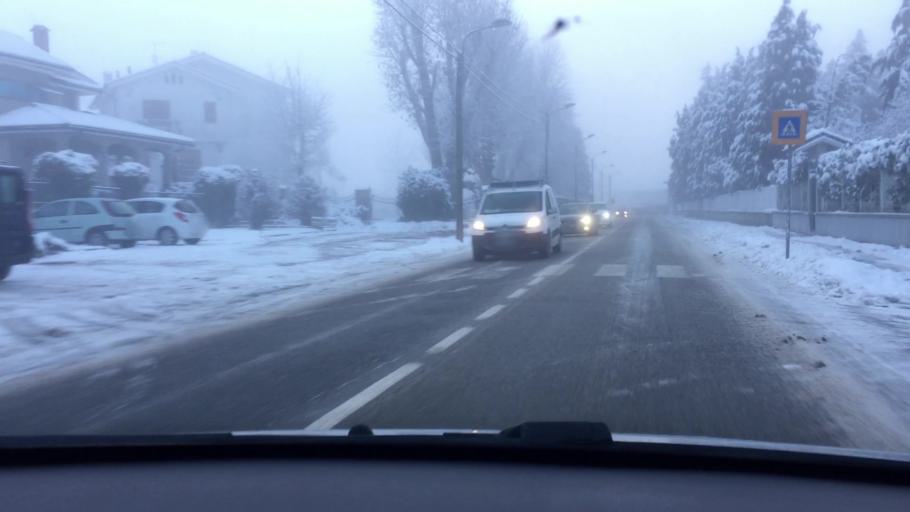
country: IT
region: Piedmont
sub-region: Provincia di Torino
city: Scalenghe
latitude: 44.8903
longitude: 7.4942
